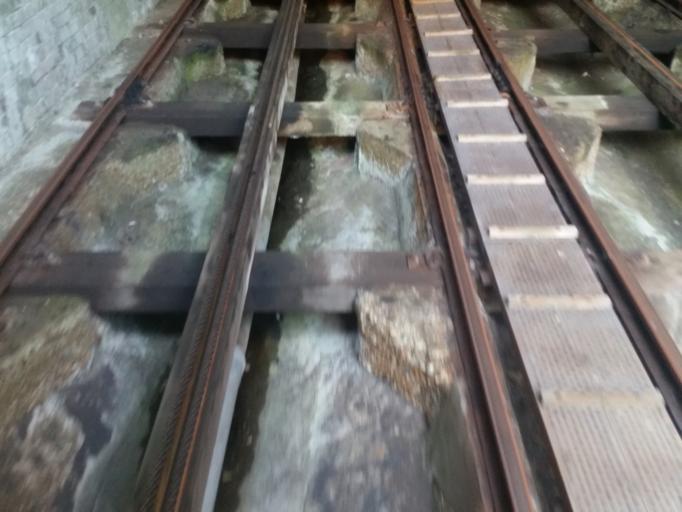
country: GB
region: England
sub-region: East Sussex
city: Hastings
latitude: 50.8558
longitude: 0.5876
